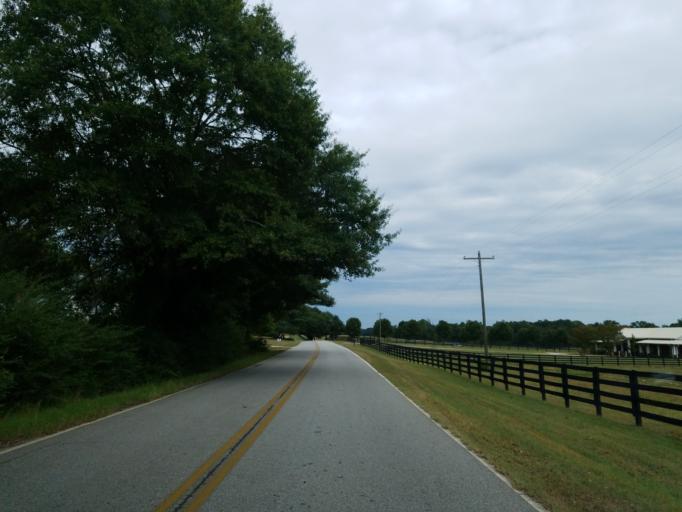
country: US
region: Georgia
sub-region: Lamar County
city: Barnesville
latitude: 33.0083
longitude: -84.0975
